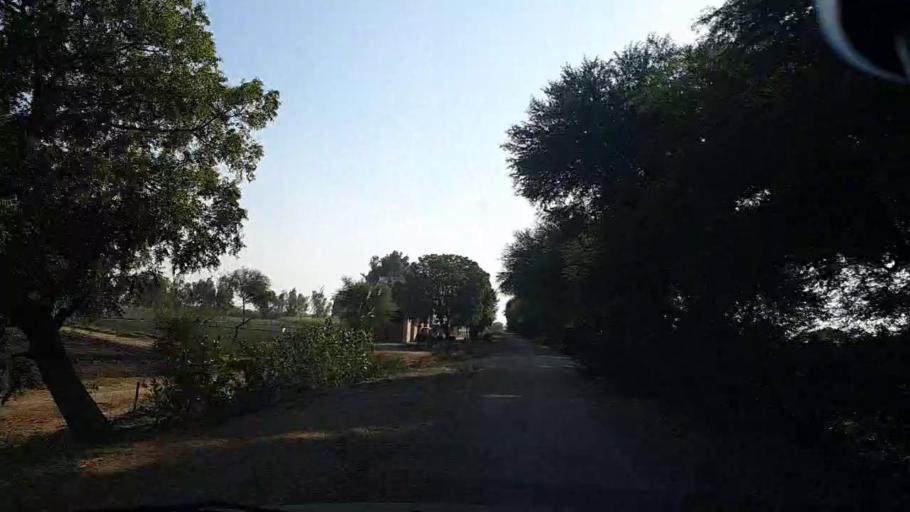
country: PK
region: Sindh
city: Chuhar Jamali
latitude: 24.5630
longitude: 68.0403
